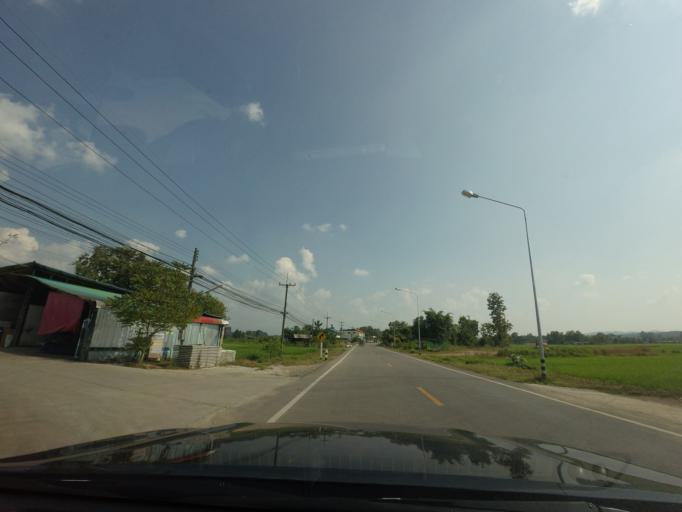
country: TH
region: Nan
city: Santi Suk
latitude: 18.9311
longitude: 100.9297
